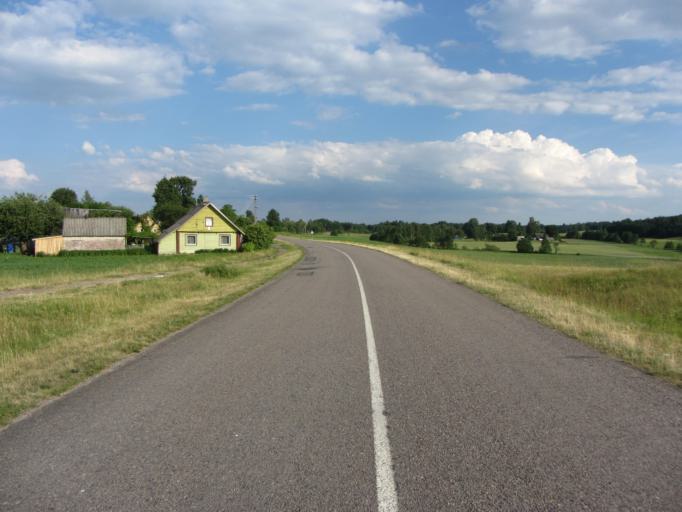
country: LT
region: Alytaus apskritis
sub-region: Alytaus rajonas
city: Daugai
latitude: 54.4388
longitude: 24.2163
